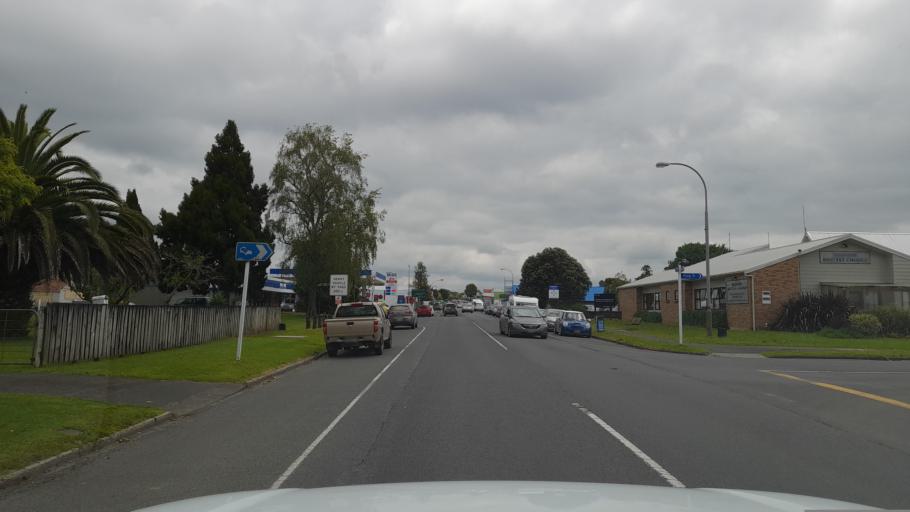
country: NZ
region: Northland
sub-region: Far North District
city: Waimate North
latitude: -35.4048
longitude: 173.8055
